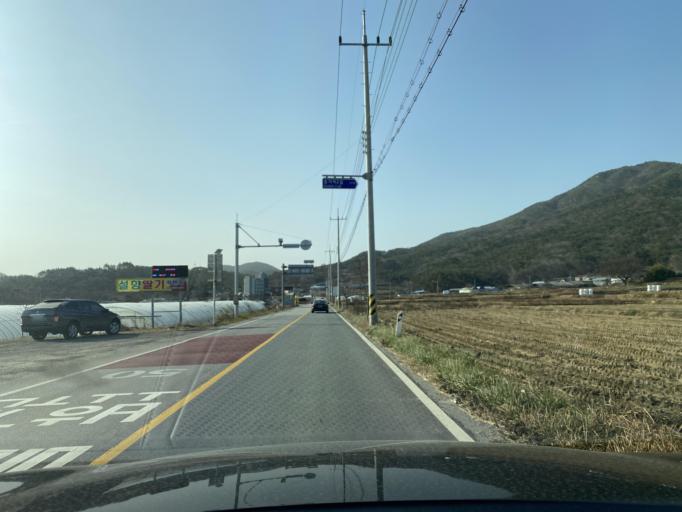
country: KR
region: Chungcheongnam-do
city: Hongsung
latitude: 36.6792
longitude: 126.6455
